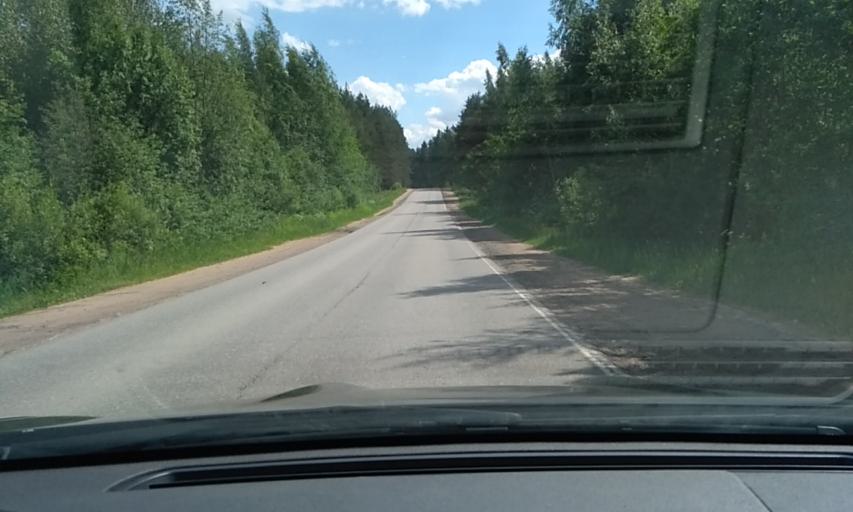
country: RU
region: Leningrad
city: Imeni Sverdlova
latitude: 59.8442
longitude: 30.6883
